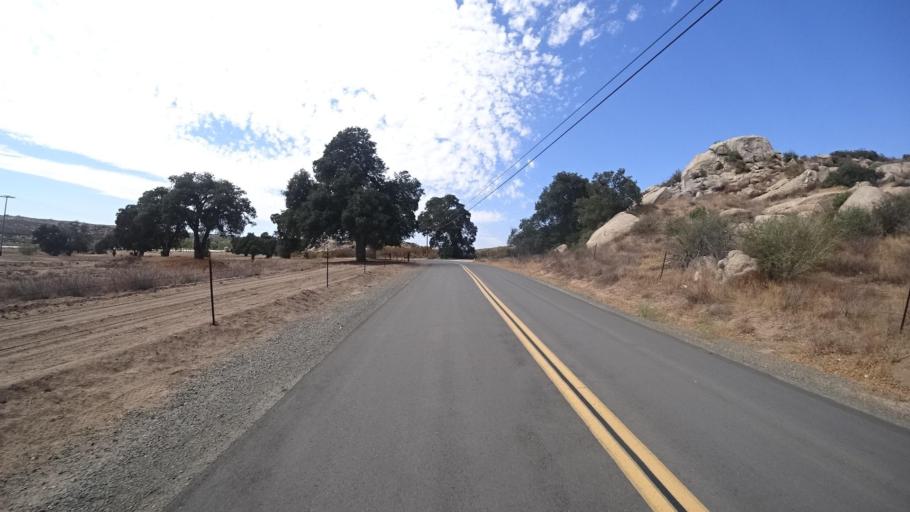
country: MX
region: Baja California
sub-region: Tecate
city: Cereso del Hongo
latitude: 32.6443
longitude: -116.2802
